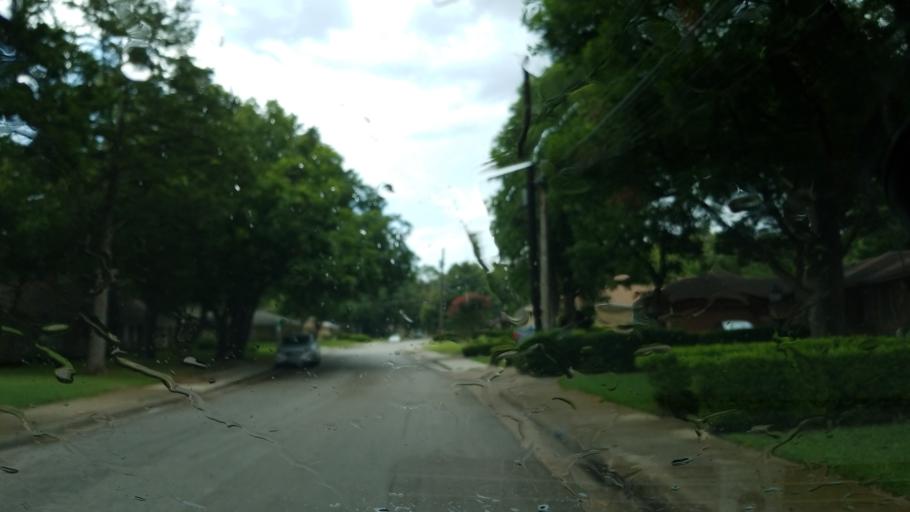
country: US
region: Texas
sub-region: Dallas County
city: Duncanville
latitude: 32.6726
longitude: -96.8372
